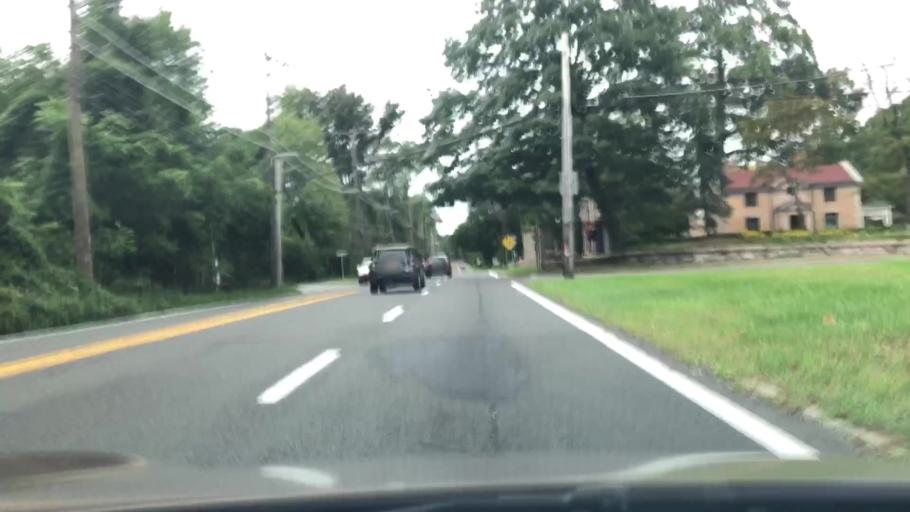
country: US
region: New York
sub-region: Westchester County
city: Sleepy Hollow
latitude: 41.1233
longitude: -73.8618
